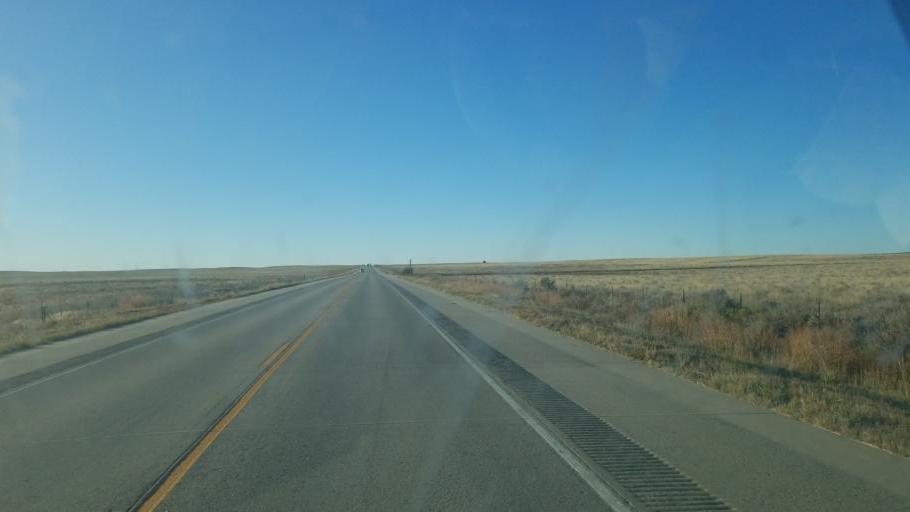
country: US
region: Colorado
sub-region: Kiowa County
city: Eads
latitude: 38.5588
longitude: -102.7862
